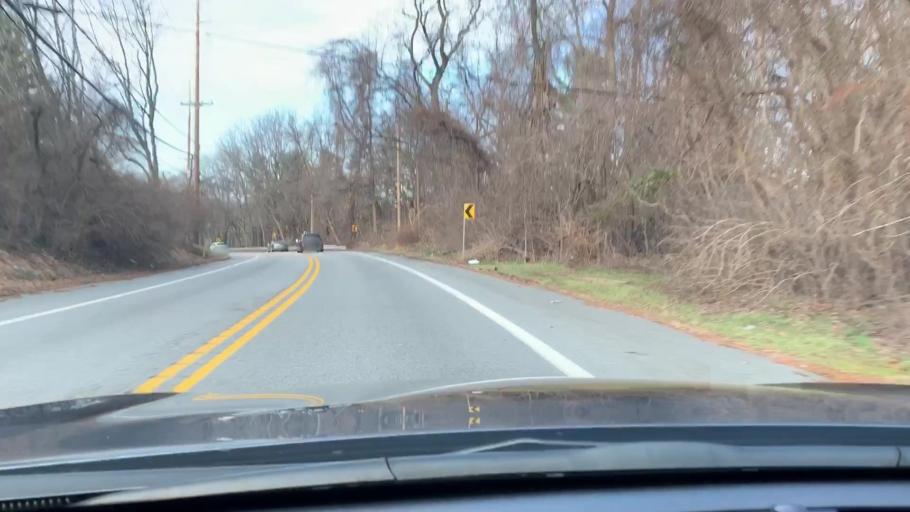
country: US
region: Pennsylvania
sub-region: Chester County
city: Berwyn
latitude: 40.0148
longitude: -75.4336
